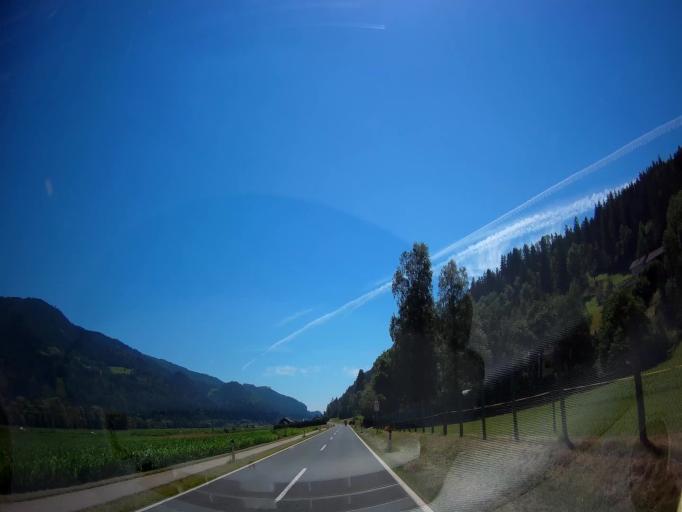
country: AT
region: Carinthia
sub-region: Politischer Bezirk Sankt Veit an der Glan
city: Micheldorf
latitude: 46.9376
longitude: 14.4231
